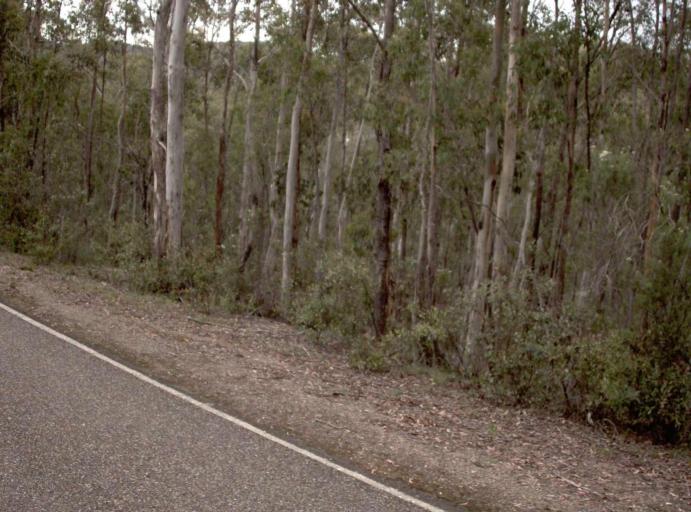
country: AU
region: Victoria
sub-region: East Gippsland
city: Bairnsdale
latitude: -37.6473
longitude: 147.2771
